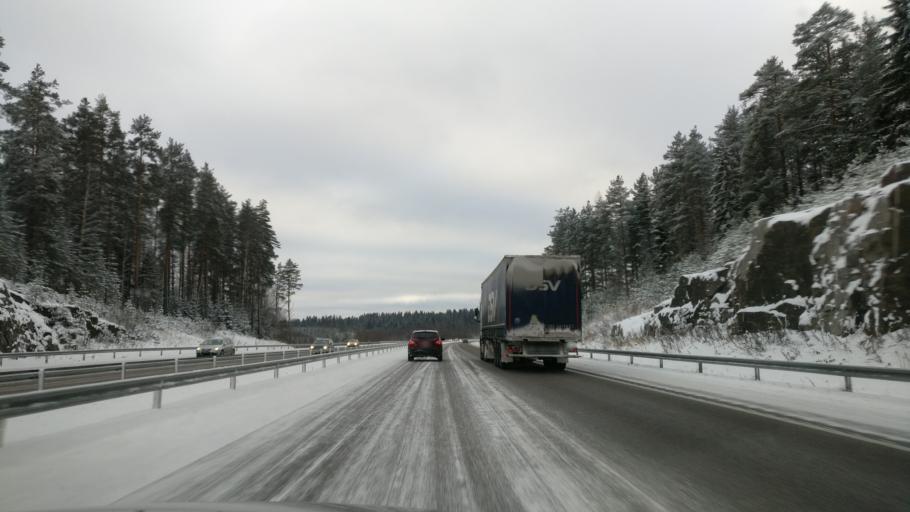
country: FI
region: Paijanne Tavastia
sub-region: Lahti
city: Nastola
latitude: 61.0103
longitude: 25.8170
